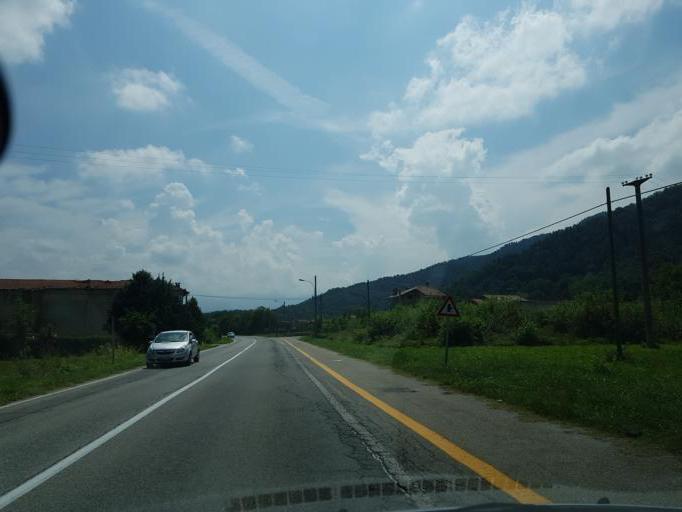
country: IT
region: Piedmont
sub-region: Provincia di Cuneo
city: Vignolo
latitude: 44.3680
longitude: 7.4741
